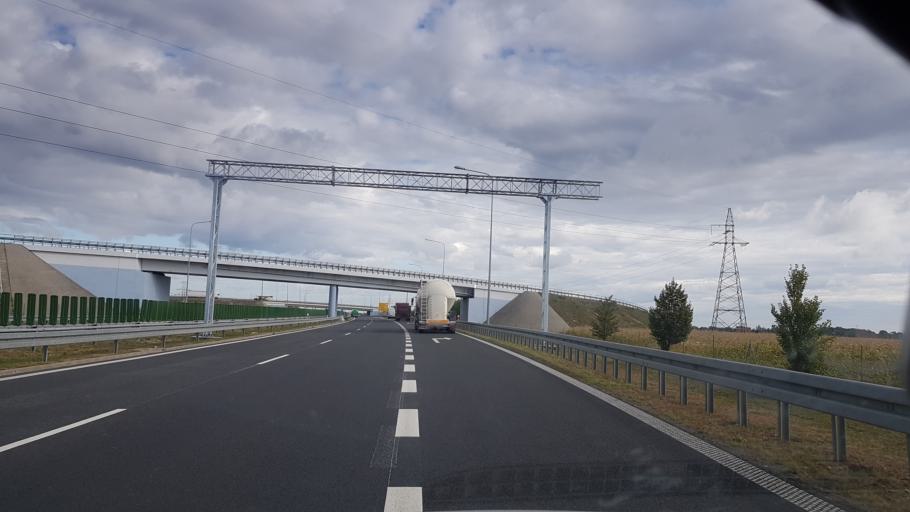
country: PL
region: Greater Poland Voivodeship
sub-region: Powiat poznanski
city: Komorniki
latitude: 52.3427
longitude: 16.7514
